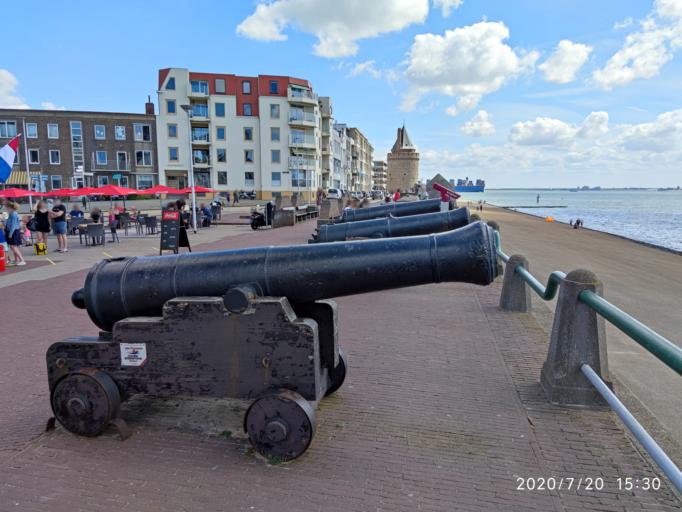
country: NL
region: Zeeland
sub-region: Gemeente Vlissingen
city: Vlissingen
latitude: 51.4438
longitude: 3.5681
